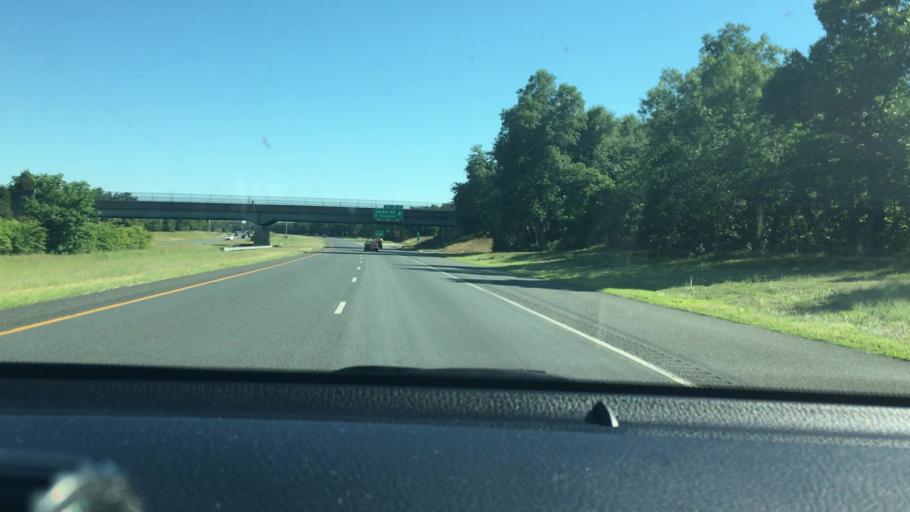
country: US
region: New Jersey
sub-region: Gloucester County
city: Newfield
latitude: 39.5233
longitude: -75.0687
